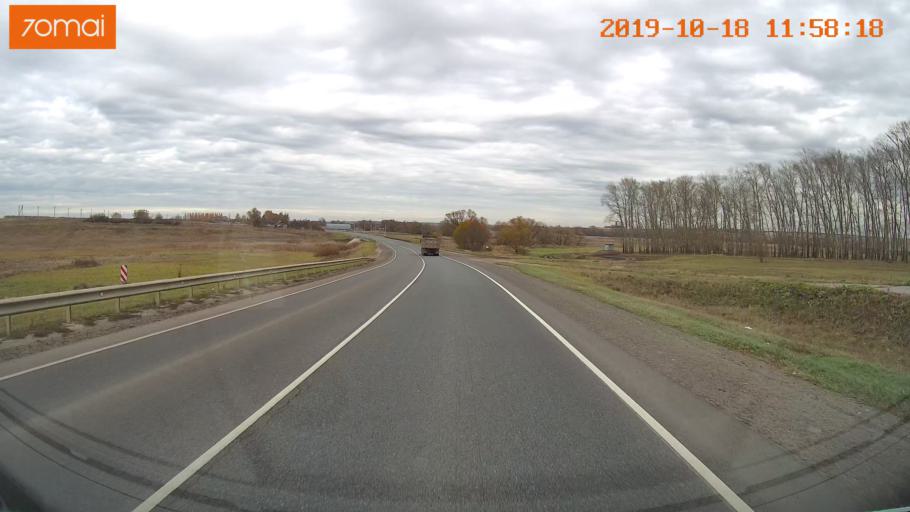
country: RU
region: Rjazan
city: Mikhaylov
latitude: 54.2702
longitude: 39.1656
